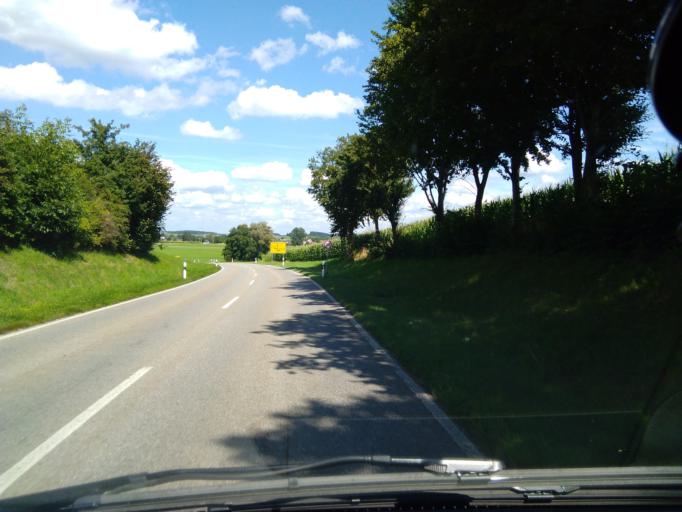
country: DE
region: Bavaria
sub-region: Upper Bavaria
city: Emmering
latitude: 47.9930
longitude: 12.0509
